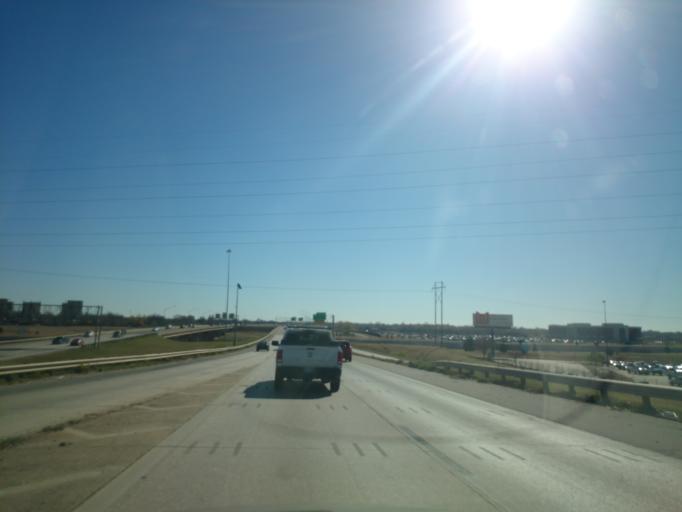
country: US
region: Oklahoma
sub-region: Oklahoma County
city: Oklahoma City
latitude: 35.4574
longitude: -97.5745
